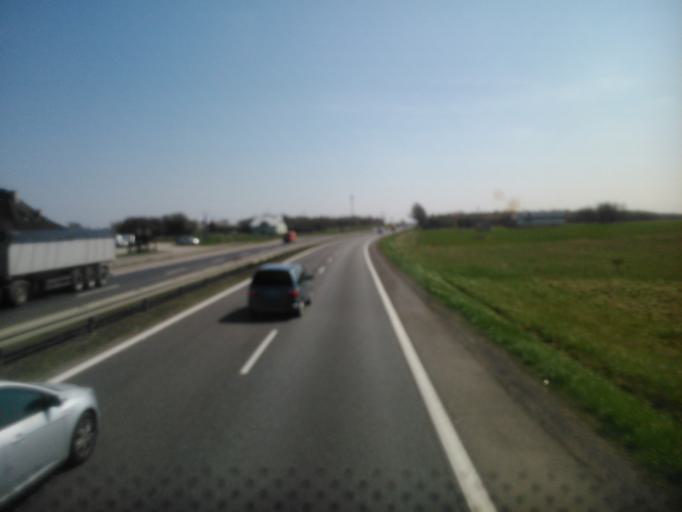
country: PL
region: Silesian Voivodeship
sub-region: Powiat myszkowski
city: Kozieglowy
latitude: 50.6148
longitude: 19.1511
